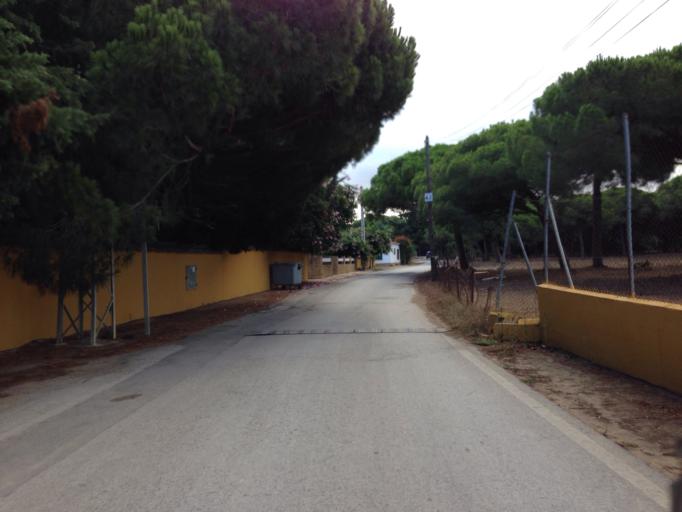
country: ES
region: Andalusia
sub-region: Provincia de Cadiz
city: Conil de la Frontera
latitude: 36.3106
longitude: -6.1124
